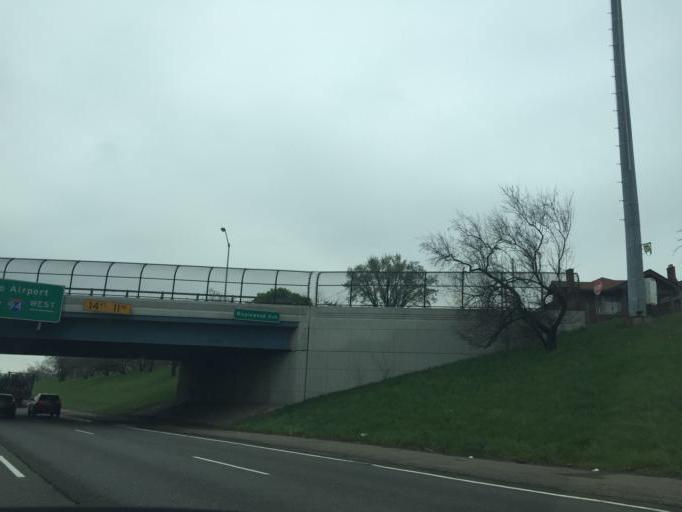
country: US
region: Michigan
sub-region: Wayne County
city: Highland Park
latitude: 42.3613
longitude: -83.1230
